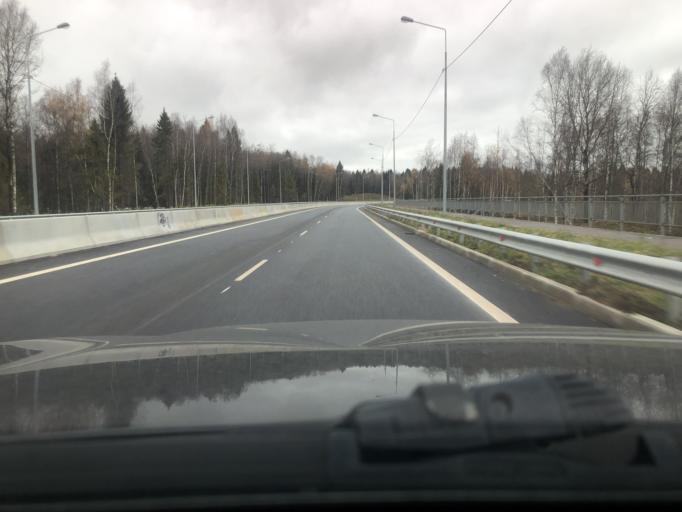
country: RU
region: Moskovskaya
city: Semkhoz
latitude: 56.3285
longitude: 38.0778
